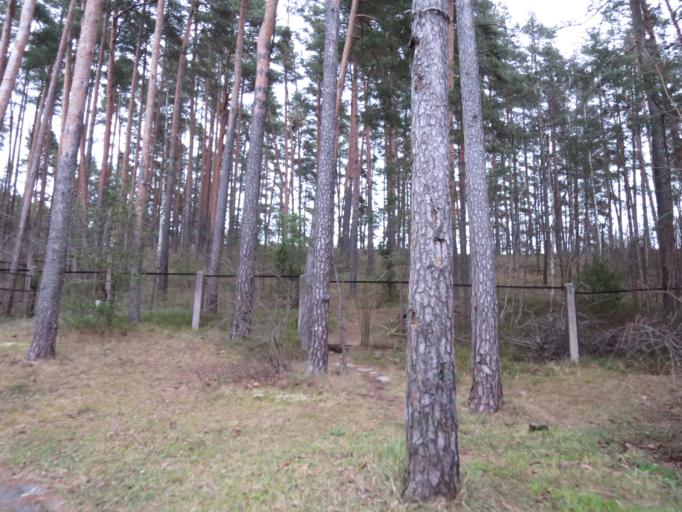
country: LV
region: Riga
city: Bergi
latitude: 56.9773
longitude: 24.3116
